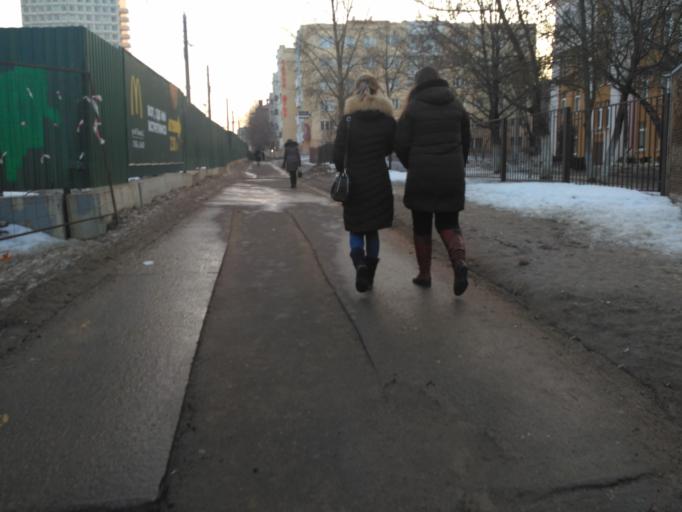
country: BY
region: Minsk
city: Minsk
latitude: 53.9085
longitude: 27.5428
